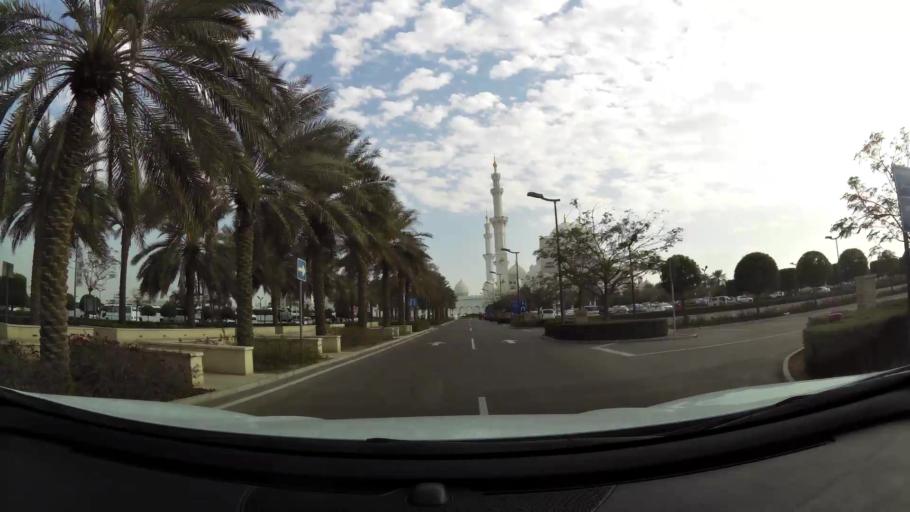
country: AE
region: Abu Dhabi
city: Abu Dhabi
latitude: 24.4155
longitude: 54.4743
